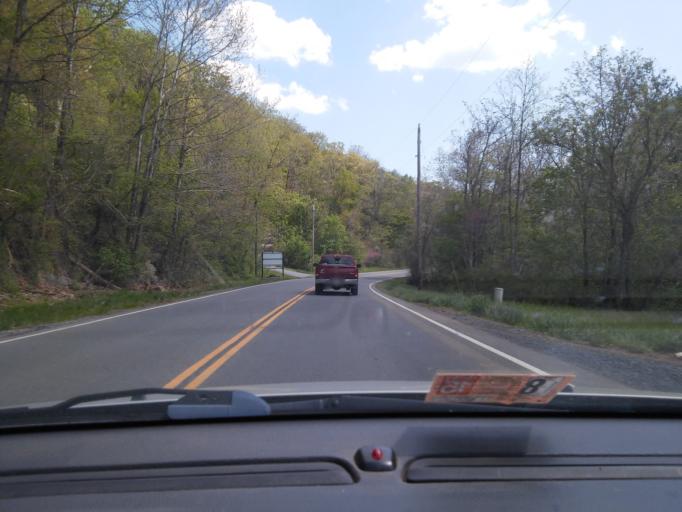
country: US
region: Virginia
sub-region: Warren County
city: Front Royal
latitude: 38.9016
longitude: -78.1831
